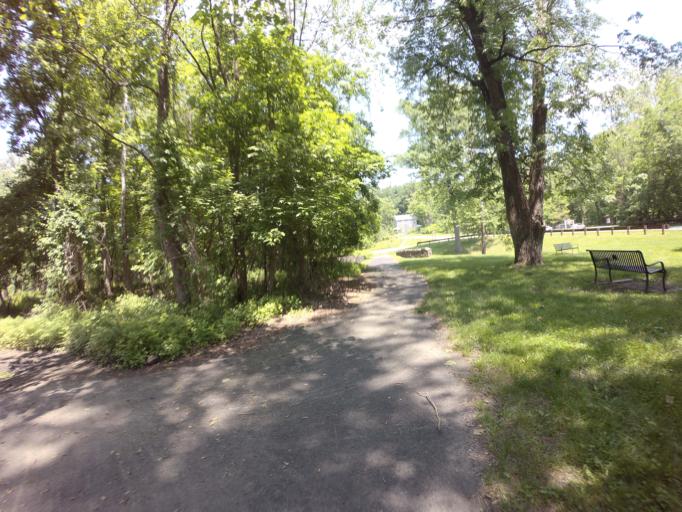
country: US
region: Maryland
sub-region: Howard County
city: Elkridge
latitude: 39.2278
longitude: -76.7226
